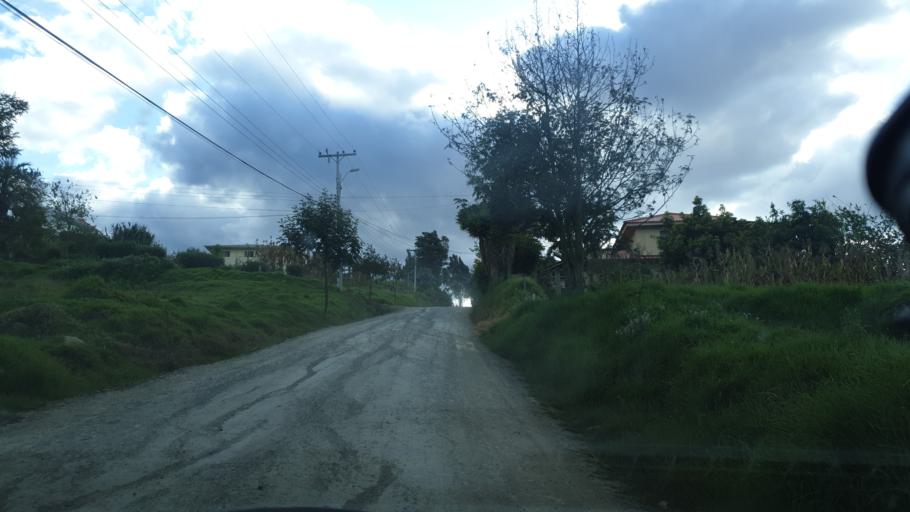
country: EC
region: Azuay
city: Cuenca
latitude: -2.9250
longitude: -78.9669
